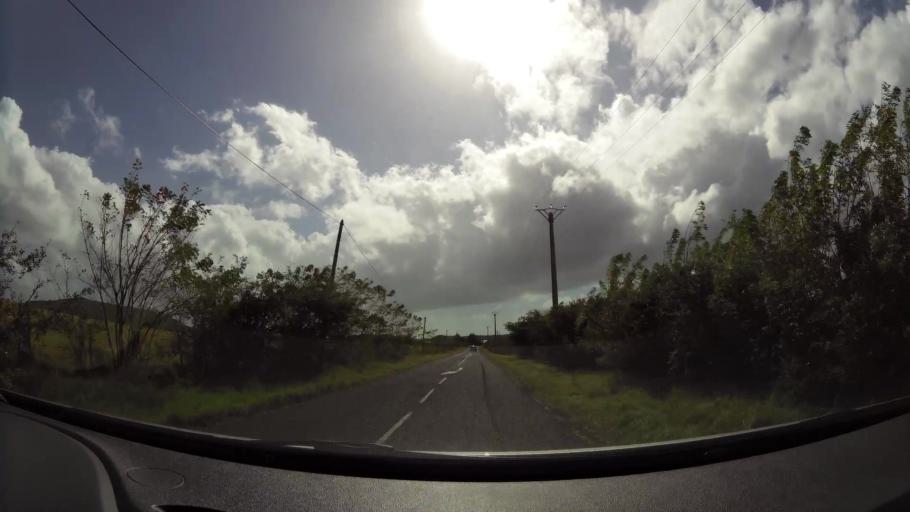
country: MQ
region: Martinique
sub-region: Martinique
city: Le Marin
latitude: 14.4090
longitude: -60.8776
